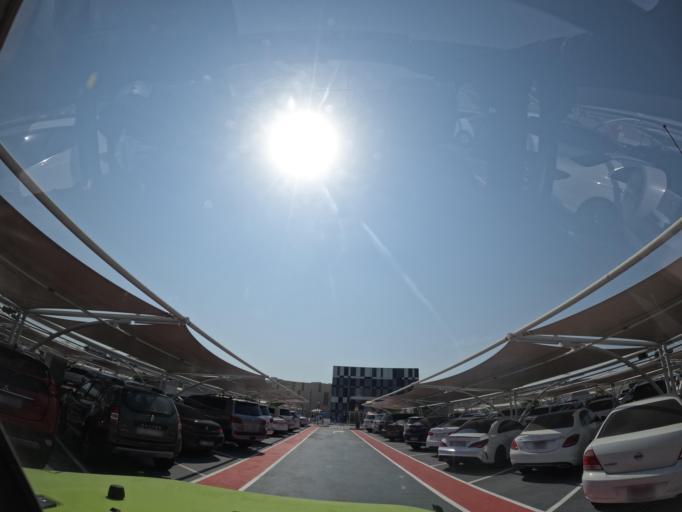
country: AE
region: Abu Dhabi
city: Abu Dhabi
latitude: 24.4896
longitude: 54.6118
